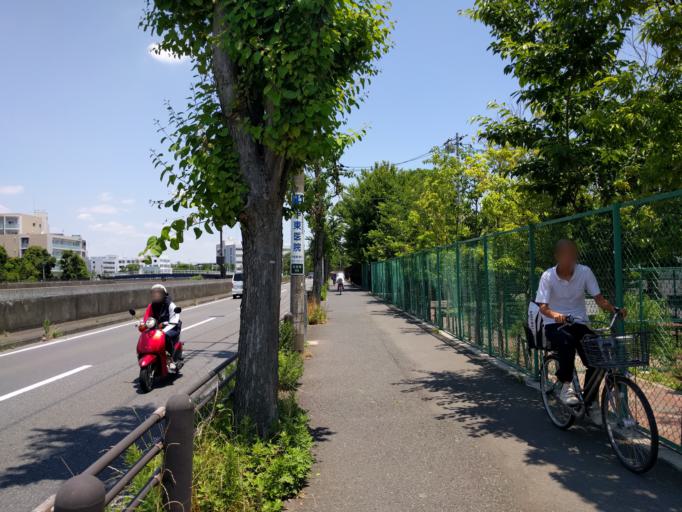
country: JP
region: Kanagawa
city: Fujisawa
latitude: 35.4016
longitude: 139.5369
